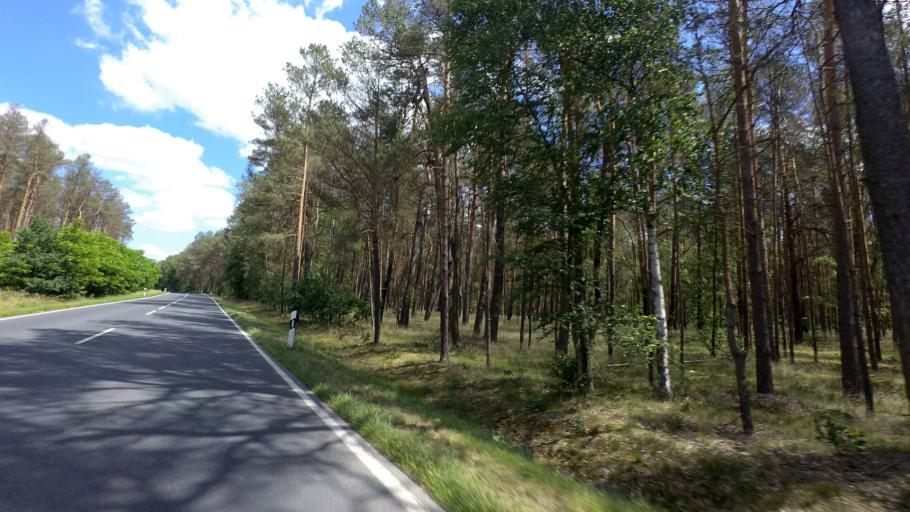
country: DE
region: Brandenburg
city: Sonnewalde
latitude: 51.7345
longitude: 13.6800
